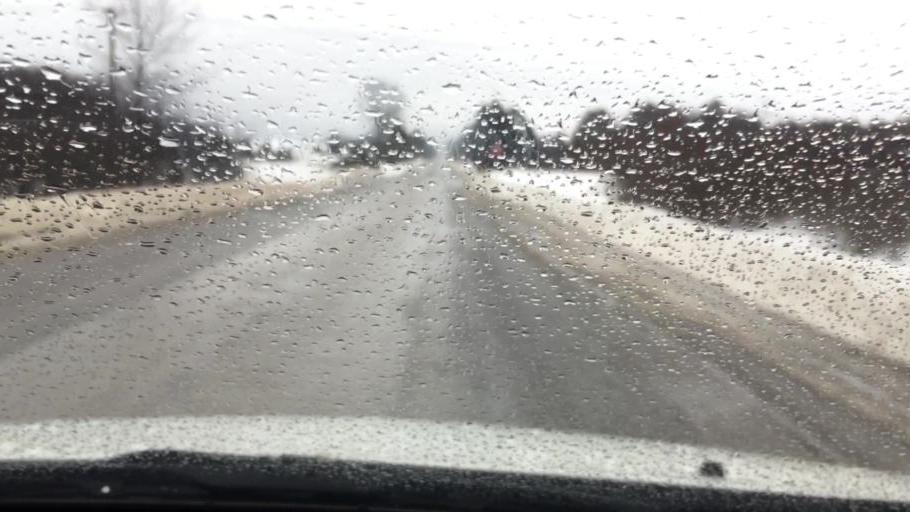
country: US
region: Michigan
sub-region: Charlevoix County
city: East Jordan
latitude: 45.1326
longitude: -85.1425
